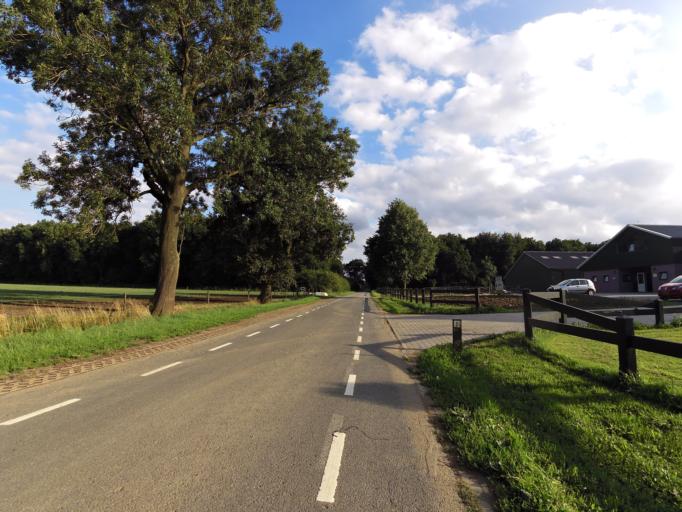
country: NL
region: Gelderland
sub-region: Gemeente Doesburg
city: Doesburg
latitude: 51.9889
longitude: 6.1613
